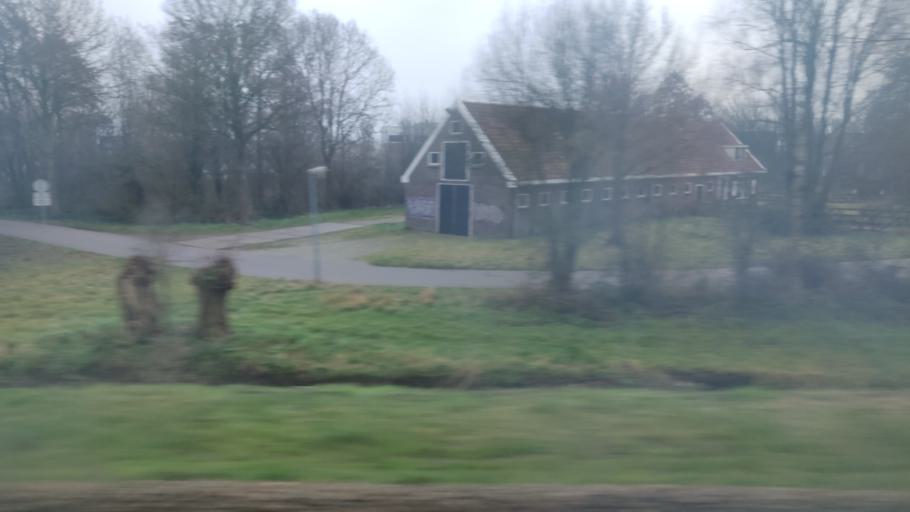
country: NL
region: North Holland
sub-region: Gemeente Langedijk
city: Broek op Langedijk
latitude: 52.6547
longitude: 4.7885
